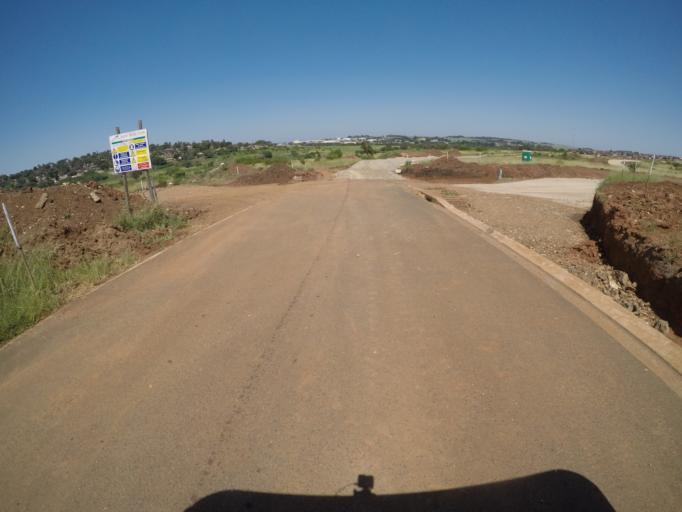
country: ZA
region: KwaZulu-Natal
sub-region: uThungulu District Municipality
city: Empangeni
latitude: -28.7663
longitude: 31.8826
